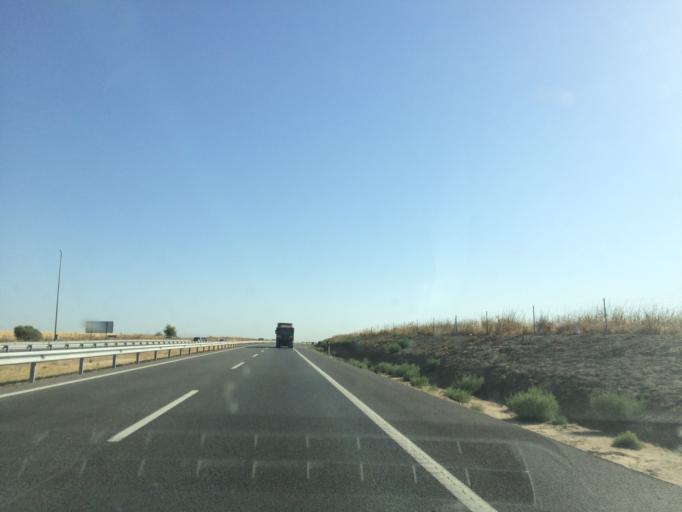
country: ES
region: Castille-La Mancha
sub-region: Province of Toledo
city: Maqueda
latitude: 40.0790
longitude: -4.3572
